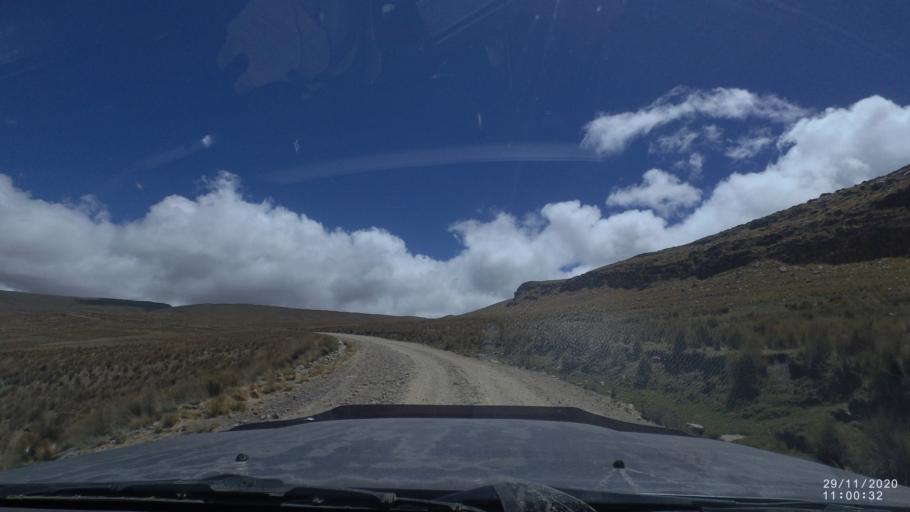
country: BO
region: Cochabamba
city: Cochabamba
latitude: -17.2036
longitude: -66.2257
